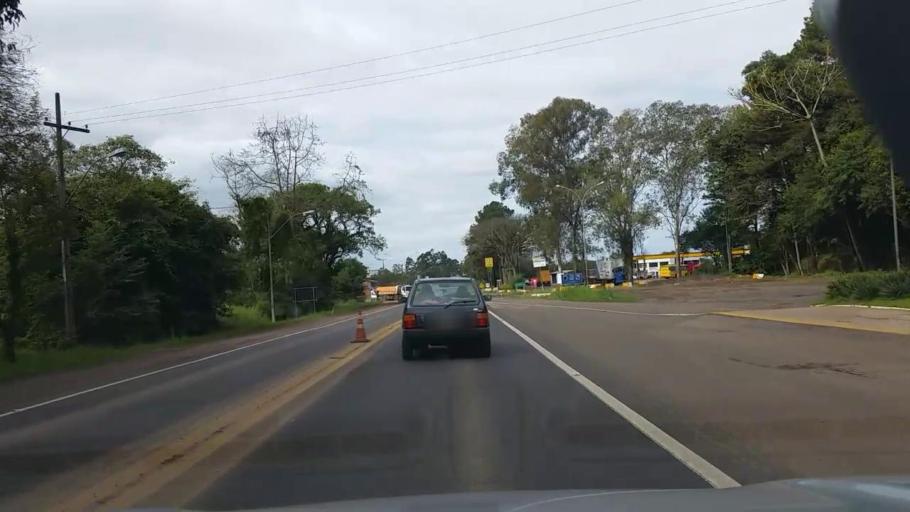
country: BR
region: Rio Grande do Sul
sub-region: Lajeado
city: Lajeado
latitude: -29.4319
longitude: -52.0115
